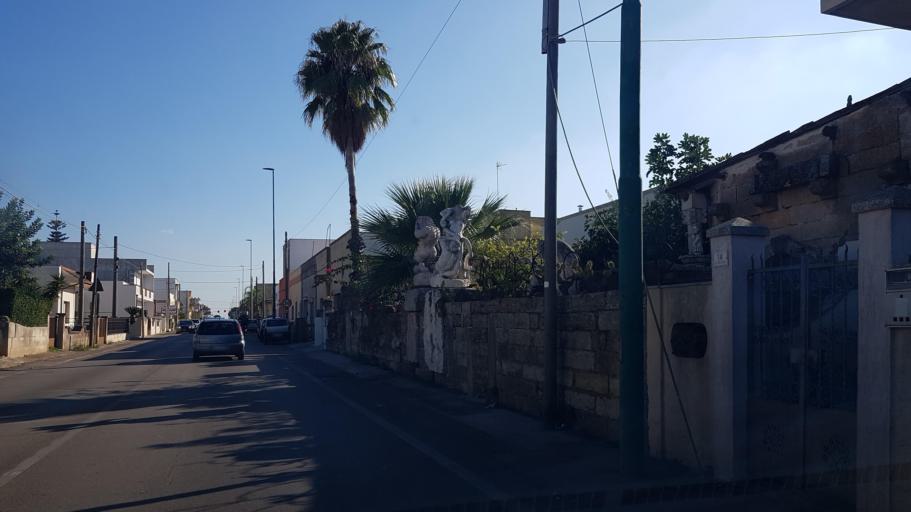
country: IT
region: Apulia
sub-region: Provincia di Lecce
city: Montesano Salentino
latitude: 39.9800
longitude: 18.3239
